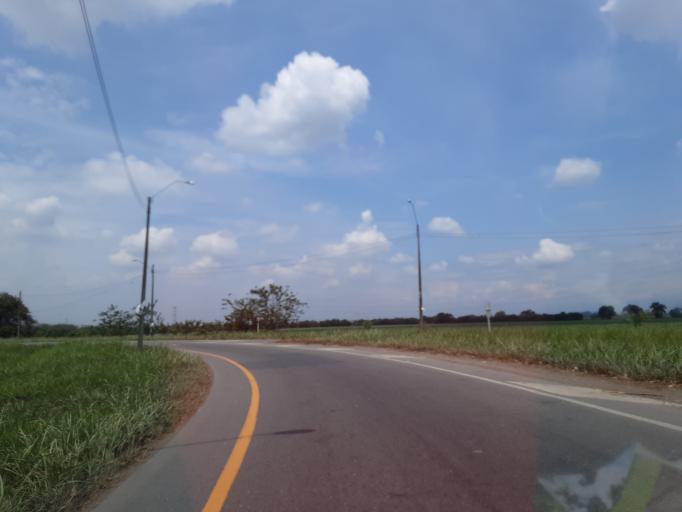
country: CO
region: Cauca
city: Puerto Tejada
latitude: 3.2336
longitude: -76.3951
